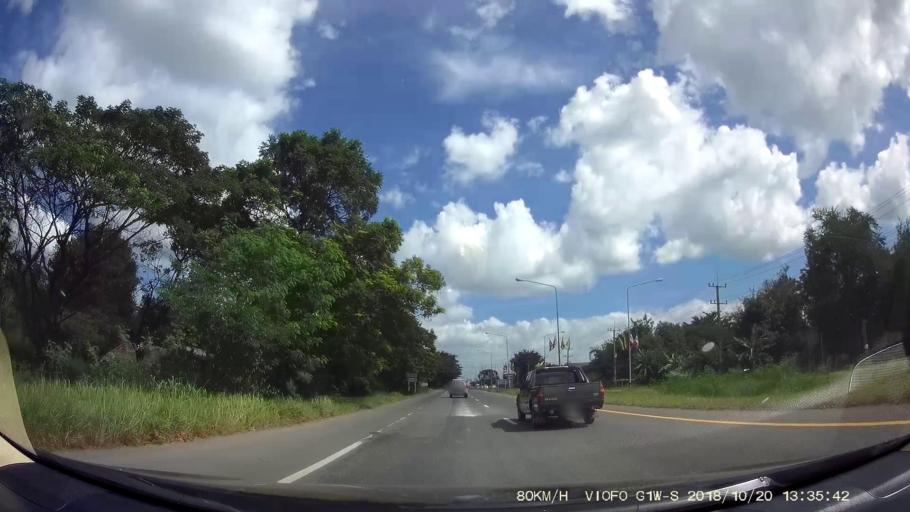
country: TH
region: Khon Kaen
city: Chum Phae
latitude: 16.5673
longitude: 102.0495
